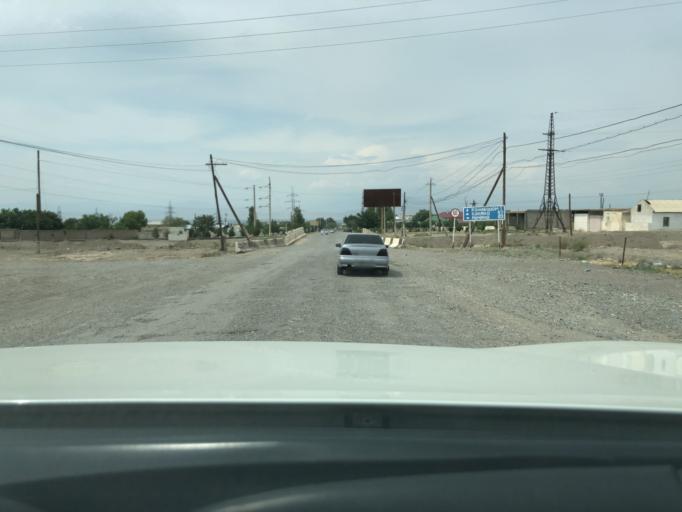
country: TJ
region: Viloyati Sughd
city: Konibodom
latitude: 40.2737
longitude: 70.4467
